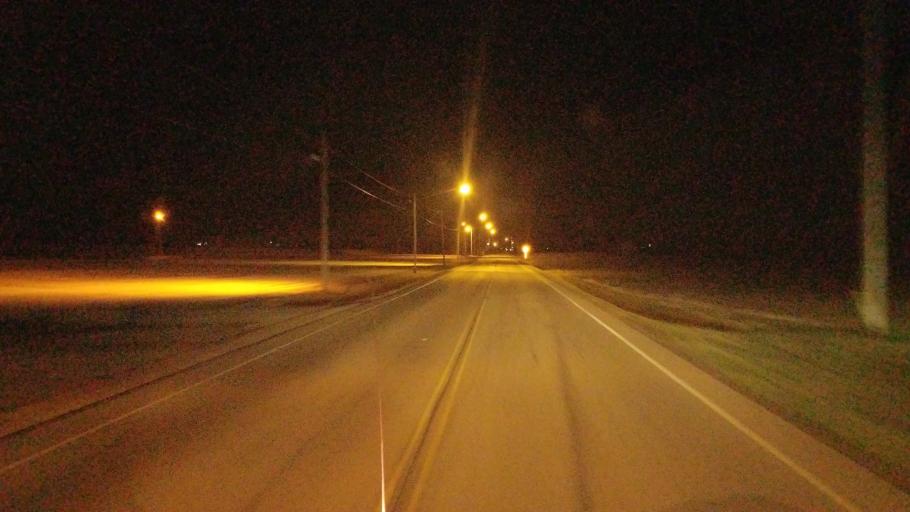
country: US
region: Ohio
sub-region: Crawford County
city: Bucyrus
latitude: 40.7867
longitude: -82.9793
